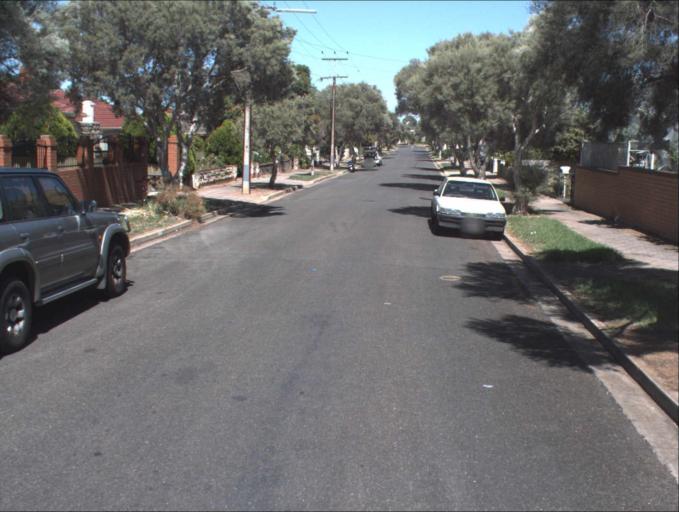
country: AU
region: South Australia
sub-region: Port Adelaide Enfield
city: Klemzig
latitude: -34.8748
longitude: 138.6374
